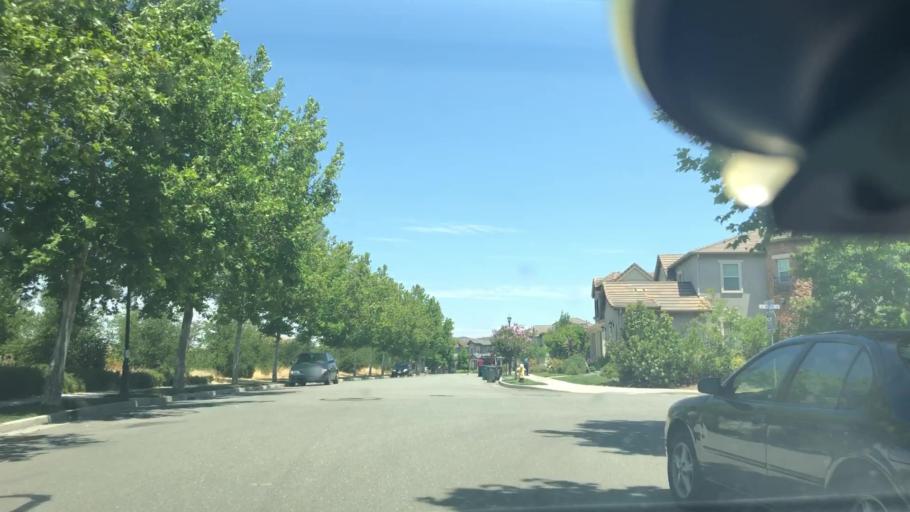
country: US
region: California
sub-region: Alameda County
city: Dublin
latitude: 37.7503
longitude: -121.8959
